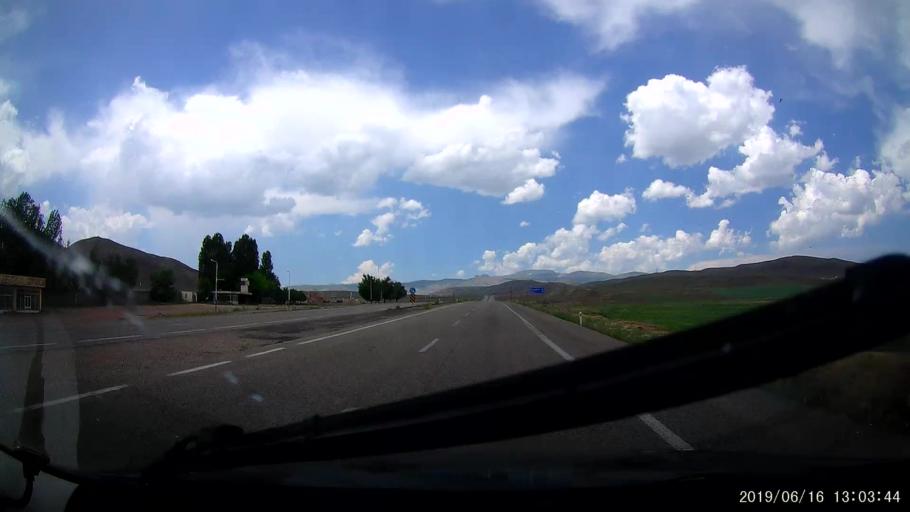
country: TR
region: Agri
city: Sulucem
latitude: 39.5846
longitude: 43.7851
